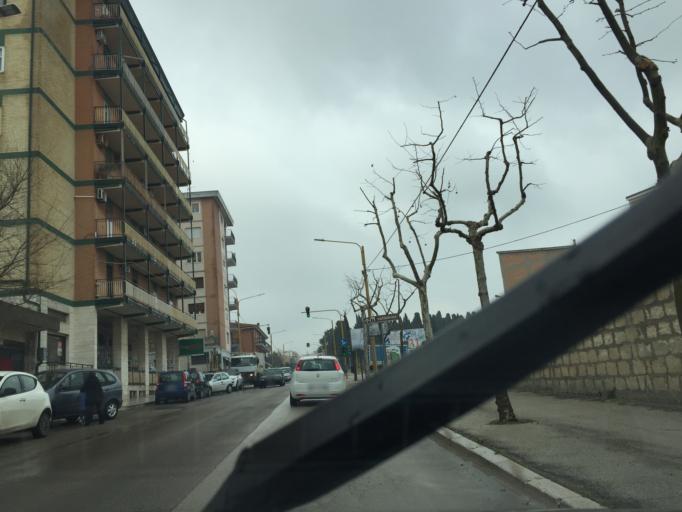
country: IT
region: Apulia
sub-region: Provincia di Foggia
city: Troia
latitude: 41.3660
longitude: 15.3219
